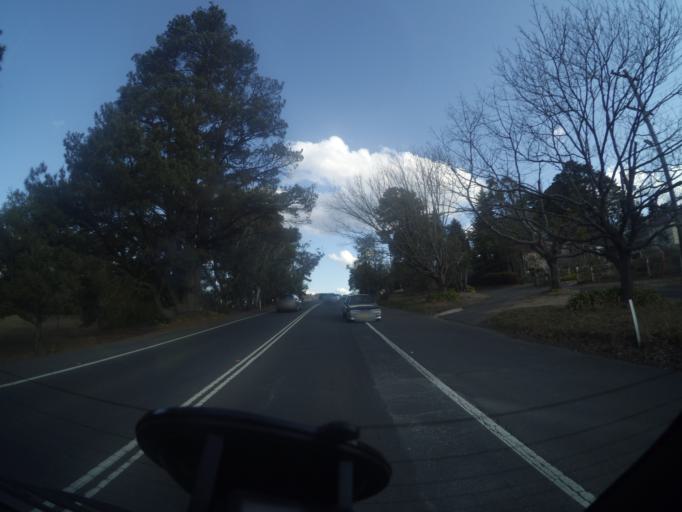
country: AU
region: New South Wales
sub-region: Blue Mountains Municipality
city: Blackheath
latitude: -33.6411
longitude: 150.2853
